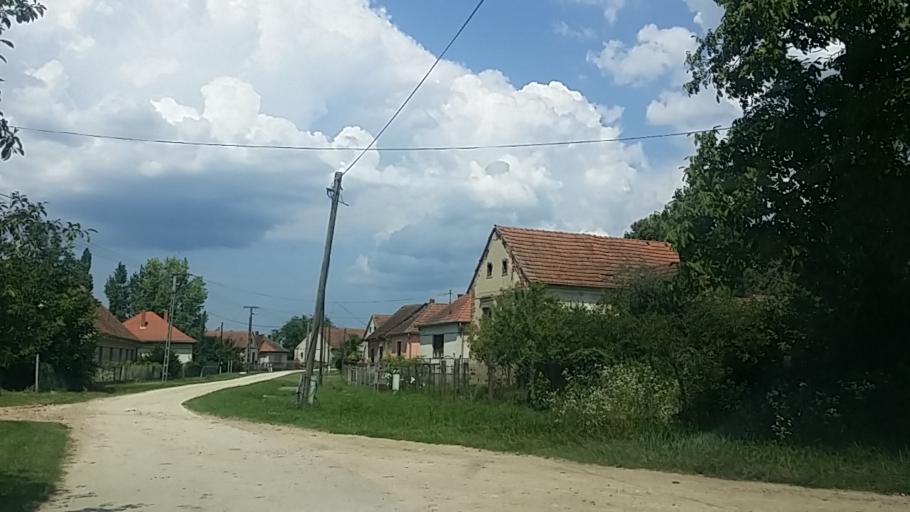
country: HR
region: Medimurska
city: Podturen
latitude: 46.5313
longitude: 16.5856
